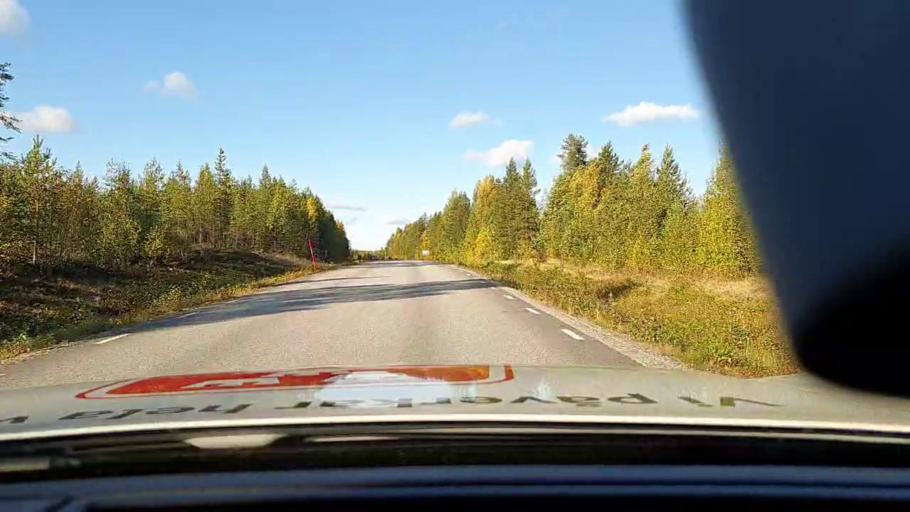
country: SE
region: Norrbotten
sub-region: Pitea Kommun
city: Norrfjarden
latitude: 65.4953
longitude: 21.4747
